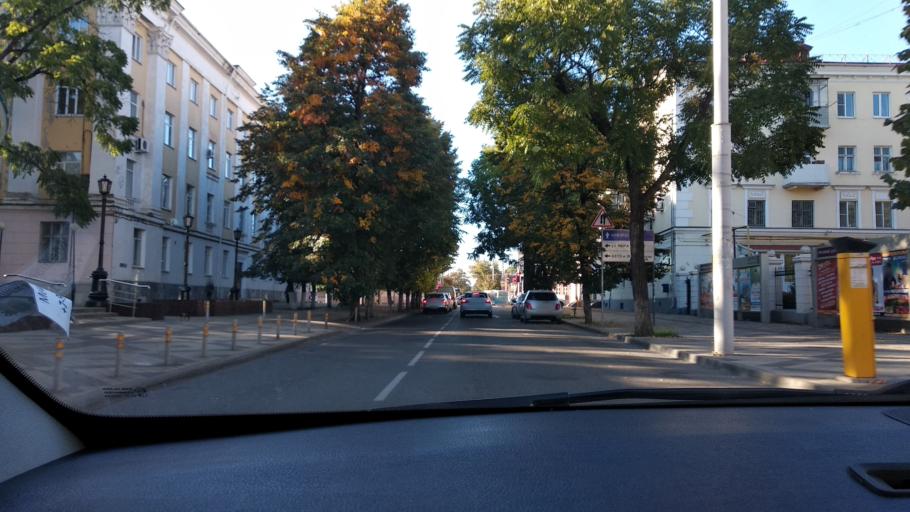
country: RU
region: Krasnodarskiy
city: Krasnodar
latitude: 45.0209
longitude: 38.9760
